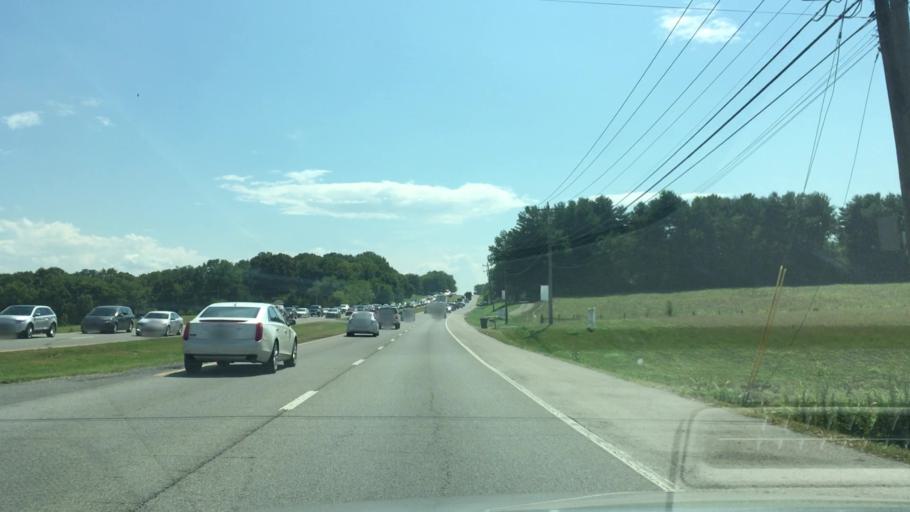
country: US
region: Tennessee
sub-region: Maury County
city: Spring Hill
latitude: 35.7027
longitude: -86.9796
